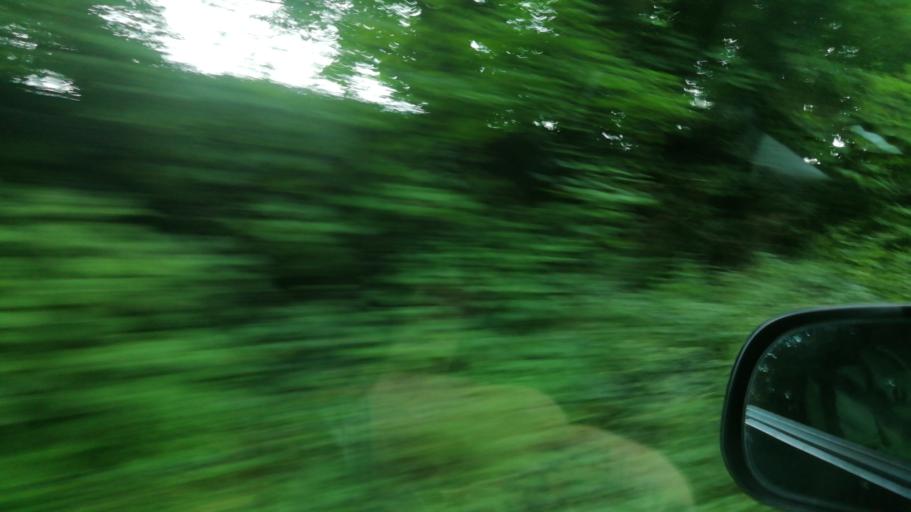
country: IE
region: Munster
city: Fethard
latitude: 52.5405
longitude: -7.6816
